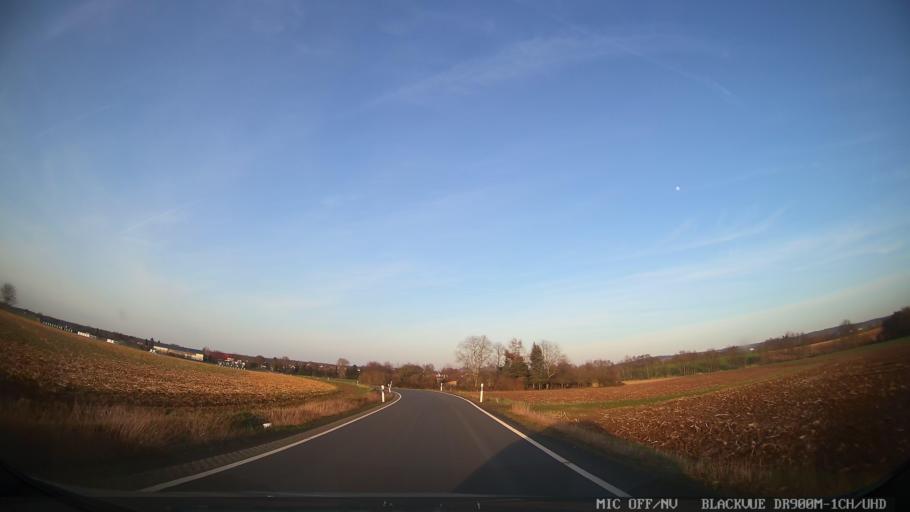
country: DE
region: Hesse
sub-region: Regierungsbezirk Darmstadt
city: Gross-Zimmern
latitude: 49.8639
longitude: 8.8817
